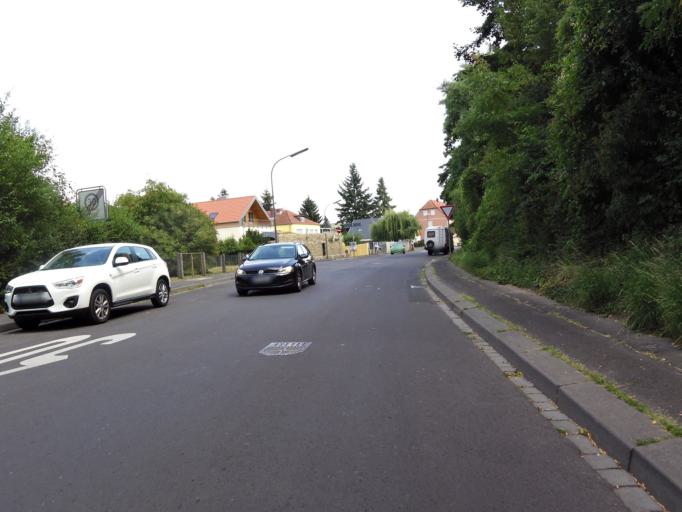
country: DE
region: Bavaria
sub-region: Regierungsbezirk Unterfranken
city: Randersacker
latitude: 49.7612
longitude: 9.9621
